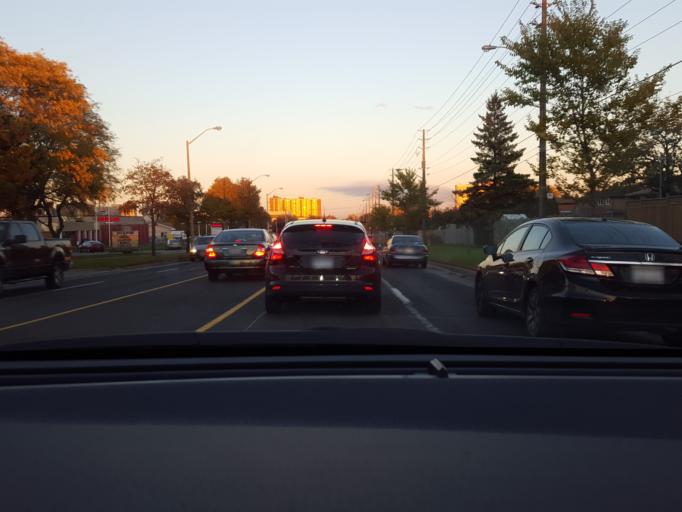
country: CA
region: Ontario
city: Scarborough
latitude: 43.7737
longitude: -79.2445
